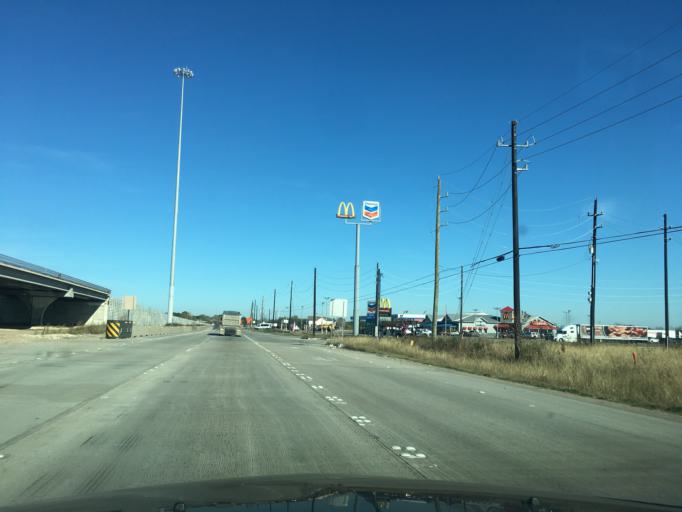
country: US
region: Texas
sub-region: Fort Bend County
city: Rosenberg
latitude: 29.5319
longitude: -95.8605
